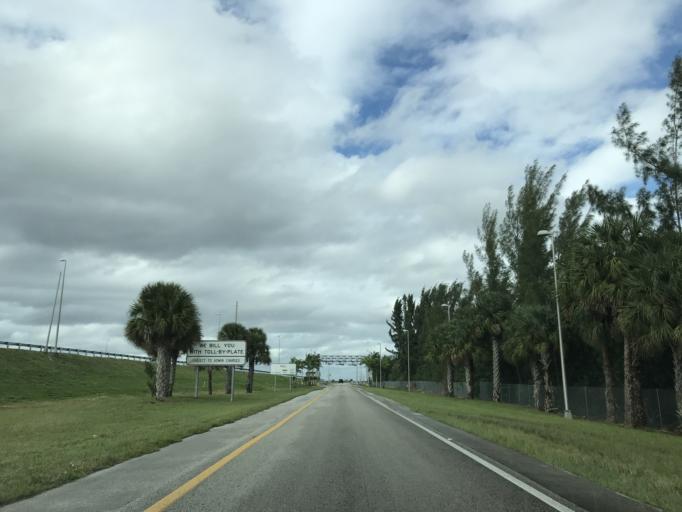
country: US
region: Florida
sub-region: Broward County
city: Coral Springs
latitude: 26.2741
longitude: -80.2958
